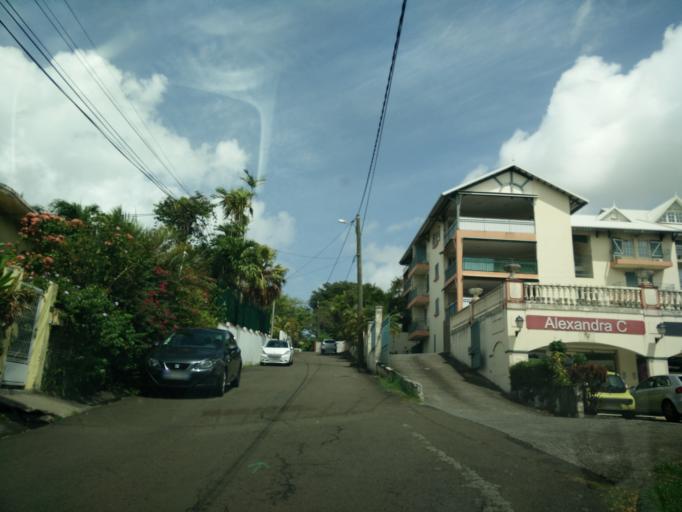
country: MQ
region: Martinique
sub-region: Martinique
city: Fort-de-France
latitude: 14.6143
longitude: -61.0784
